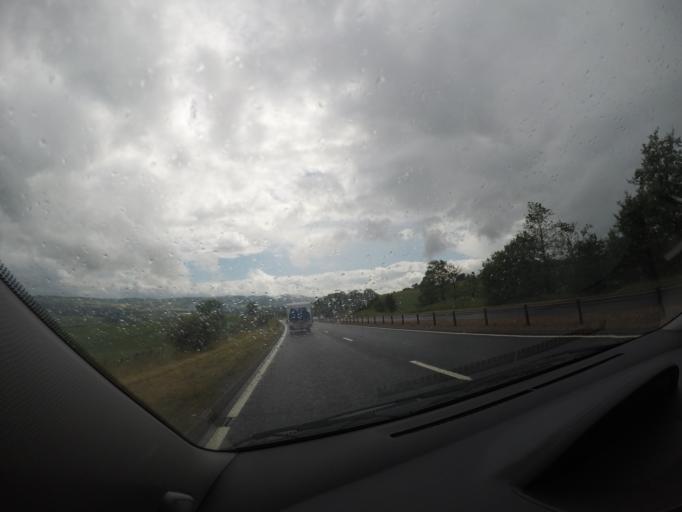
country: GB
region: Scotland
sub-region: Perth and Kinross
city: Methven
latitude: 56.3491
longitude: -3.5775
